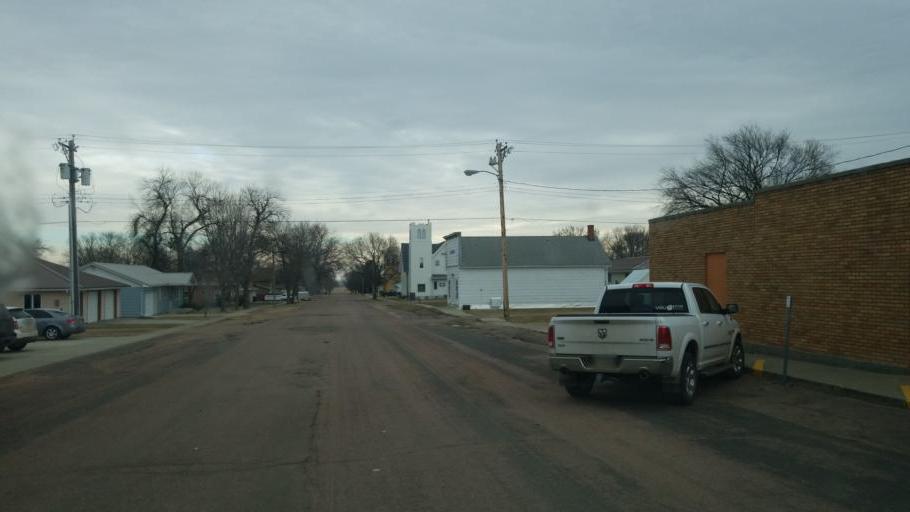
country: US
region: South Dakota
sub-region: Hutchinson County
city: Parkston
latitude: 43.2245
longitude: -97.9654
